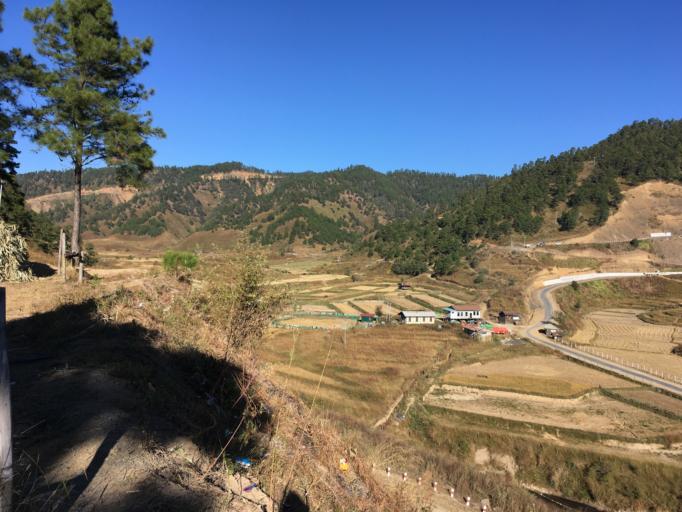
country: MM
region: Chin
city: Hakha
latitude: 22.6586
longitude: 93.5424
